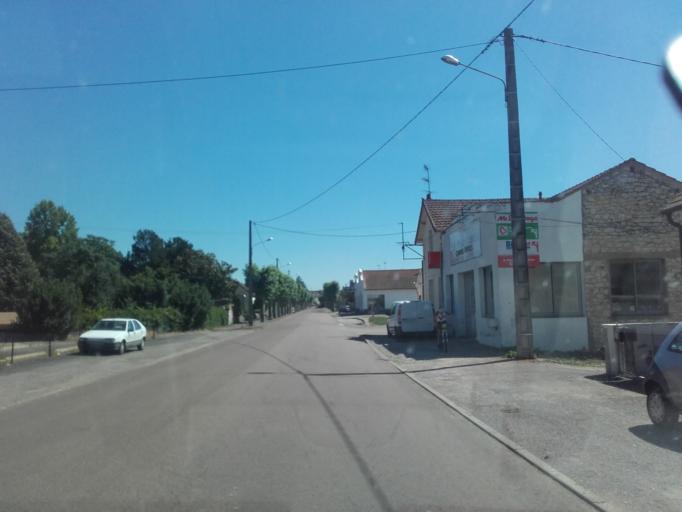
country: FR
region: Bourgogne
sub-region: Departement de Saone-et-Loire
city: Chagny
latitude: 46.9168
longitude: 4.7537
